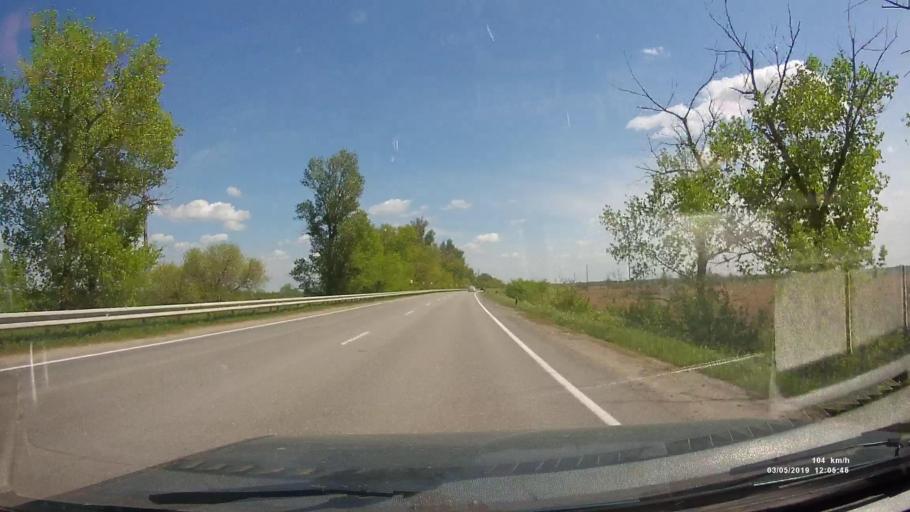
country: RU
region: Rostov
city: Bagayevskaya
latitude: 47.2861
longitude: 40.4367
